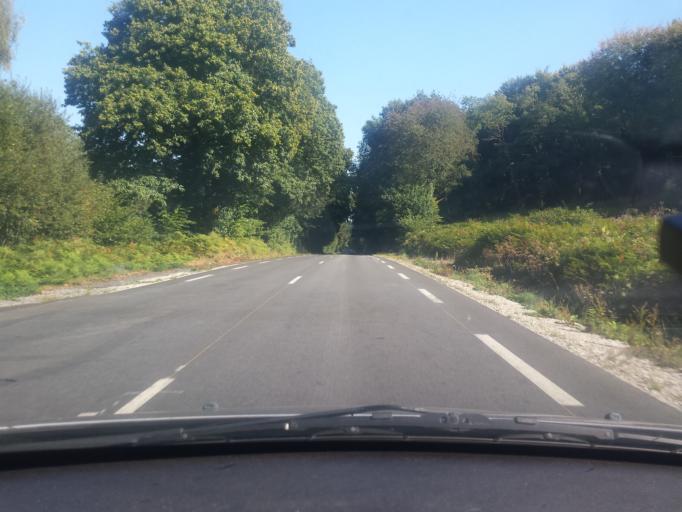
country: FR
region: Brittany
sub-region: Departement du Morbihan
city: Malguenac
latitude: 48.0988
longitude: -3.0569
